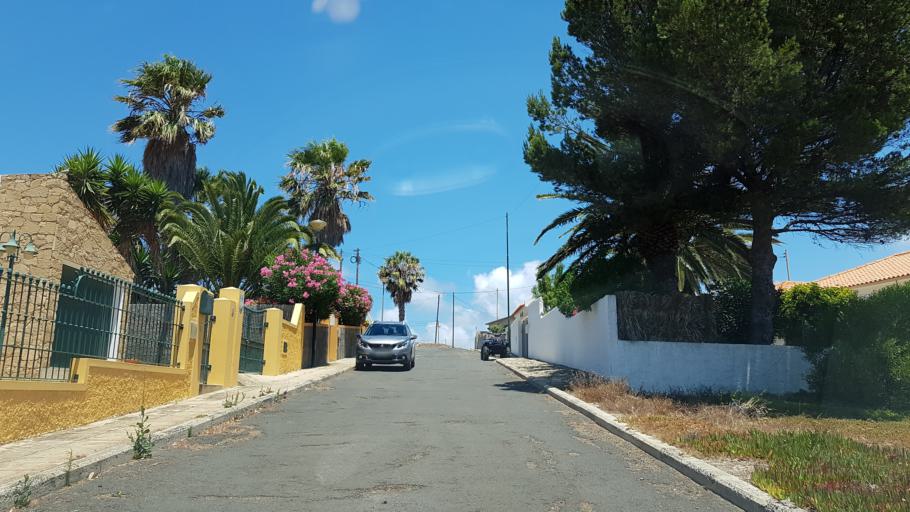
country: PT
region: Madeira
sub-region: Porto Santo
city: Vila de Porto Santo
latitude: 33.0608
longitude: -16.3528
